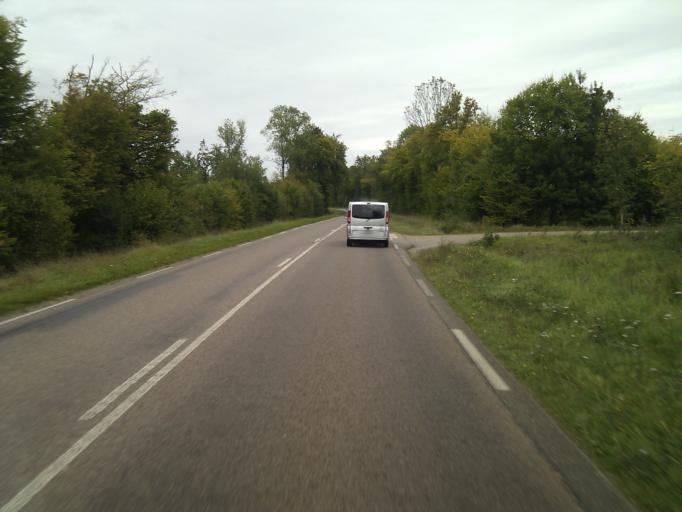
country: FR
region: Lorraine
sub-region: Departement des Vosges
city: Neufchateau
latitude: 48.3365
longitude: 5.6500
